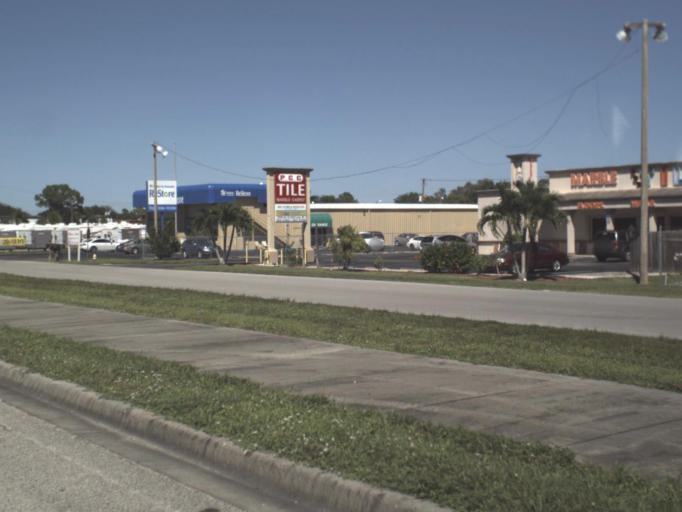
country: US
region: Florida
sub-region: Lee County
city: Villas
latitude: 26.5068
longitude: -81.8591
